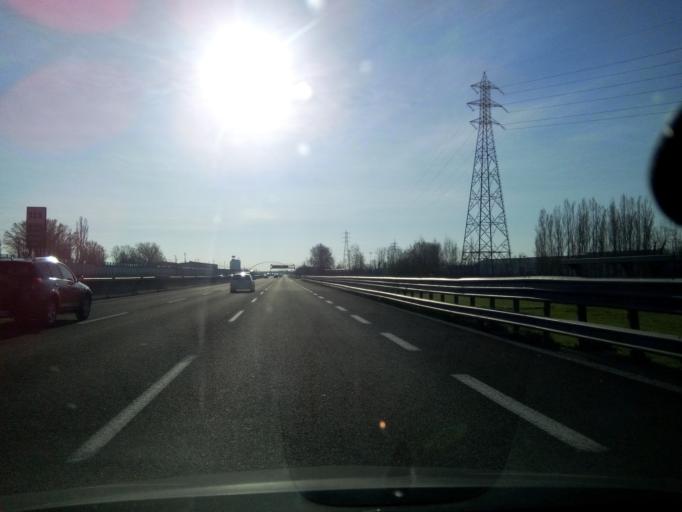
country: IT
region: Emilia-Romagna
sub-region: Provincia di Reggio Emilia
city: Roncocesi
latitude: 44.7345
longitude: 10.6060
